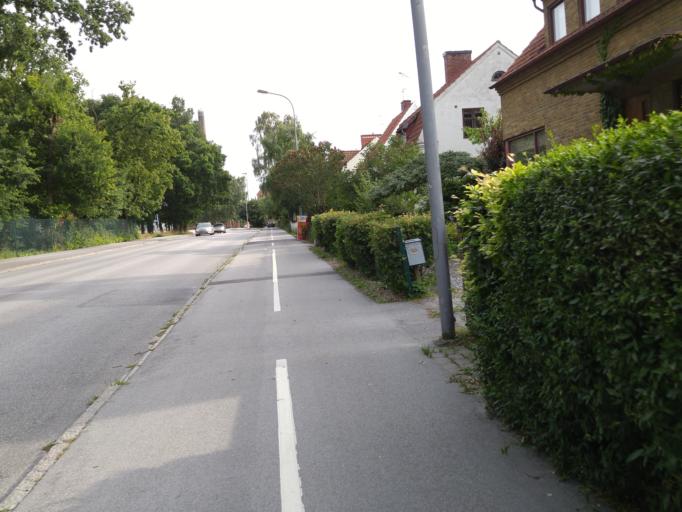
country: SE
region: Skane
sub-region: Lunds Kommun
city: Lund
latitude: 55.7173
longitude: 13.2021
